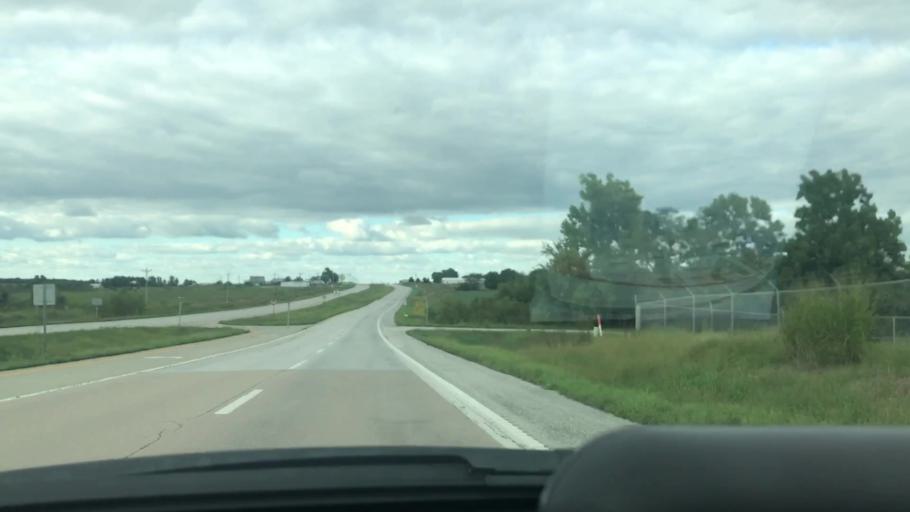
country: US
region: Missouri
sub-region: Benton County
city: Lincoln
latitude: 38.3328
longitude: -93.3413
